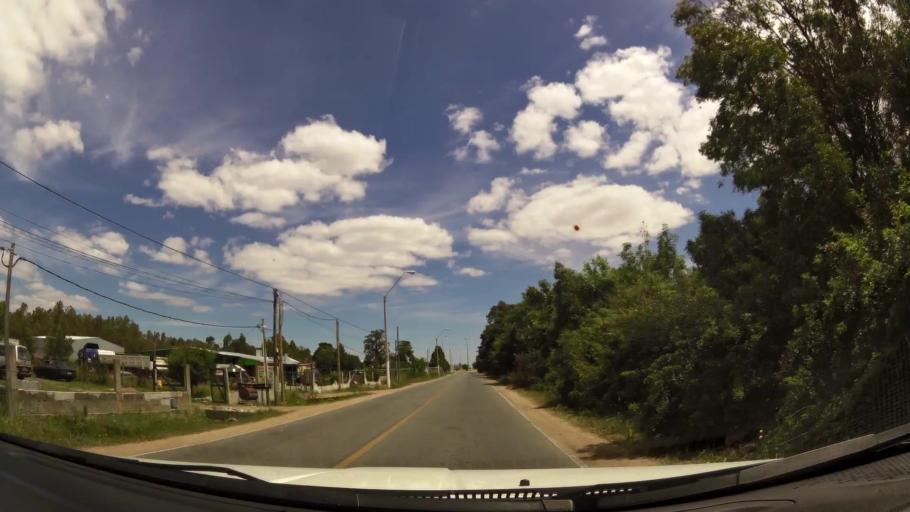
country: UY
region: San Jose
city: Delta del Tigre
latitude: -34.7371
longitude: -56.4477
